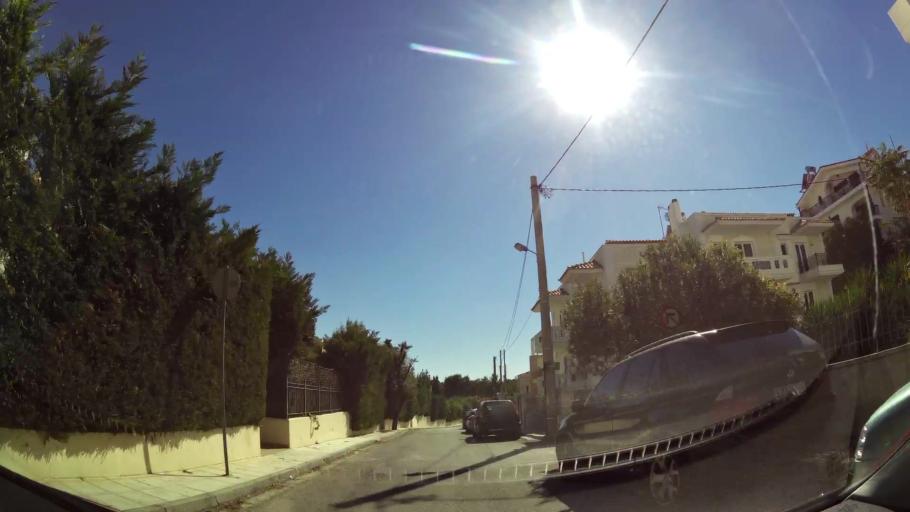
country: GR
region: Attica
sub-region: Nomarchia Anatolikis Attikis
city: Leondarion
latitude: 37.9857
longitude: 23.8617
